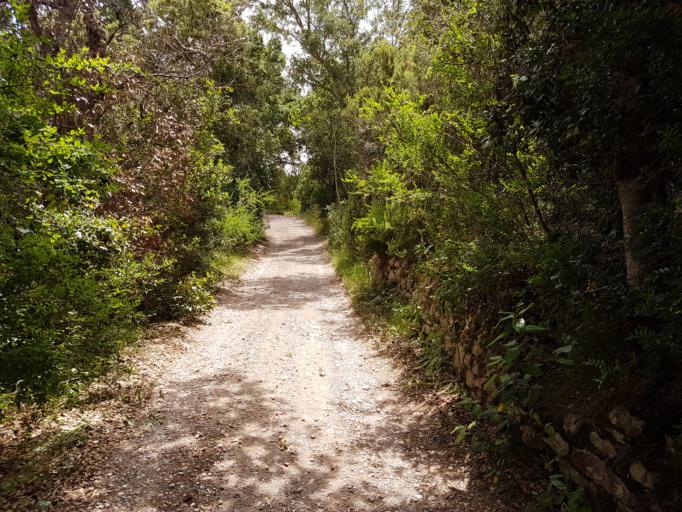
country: IT
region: Tuscany
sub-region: Provincia di Livorno
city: Portoferraio
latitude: 42.7849
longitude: 10.3501
